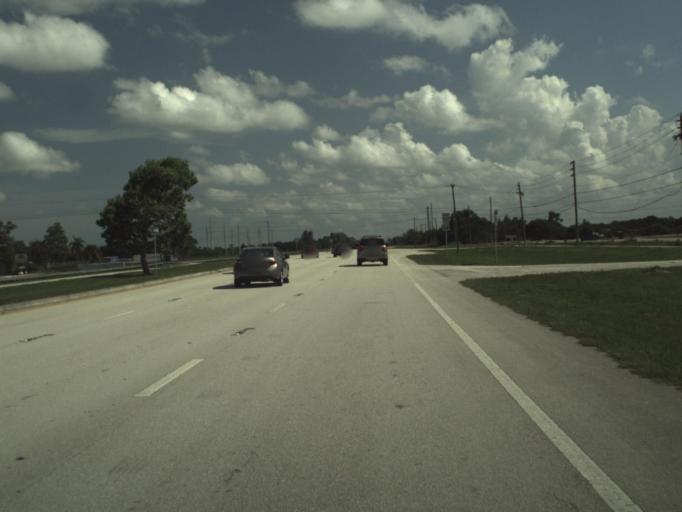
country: US
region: Florida
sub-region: Palm Beach County
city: Villages of Oriole
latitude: 26.5481
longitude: -80.2058
